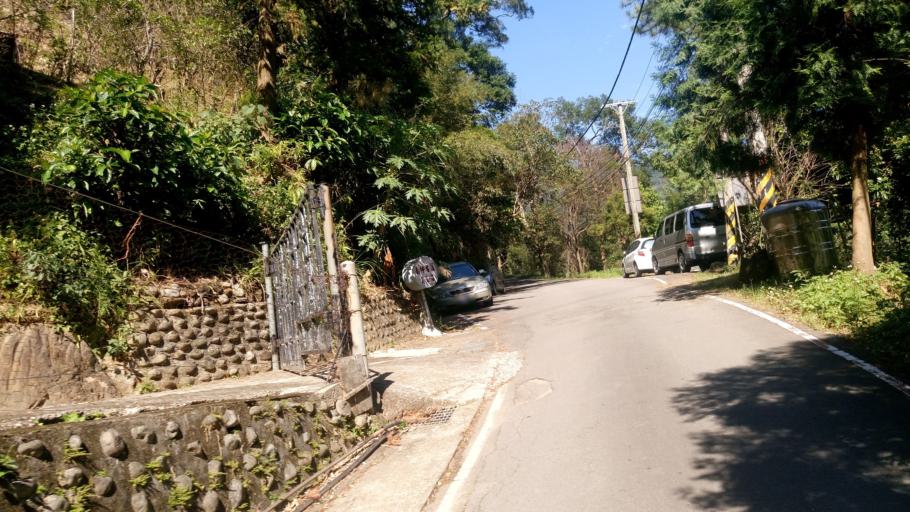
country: TW
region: Taiwan
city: Daxi
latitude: 24.7021
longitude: 121.1805
